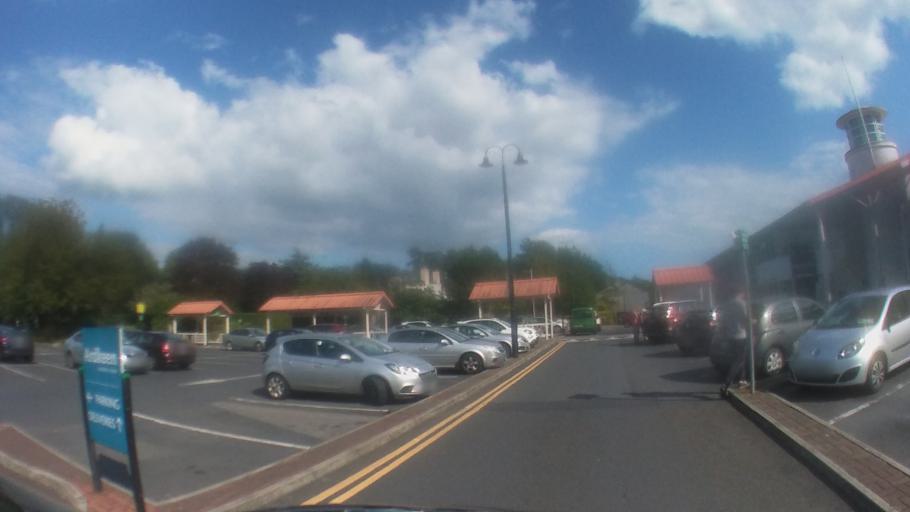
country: IE
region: Munster
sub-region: Waterford
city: Waterford
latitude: 52.2612
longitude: -7.1073
